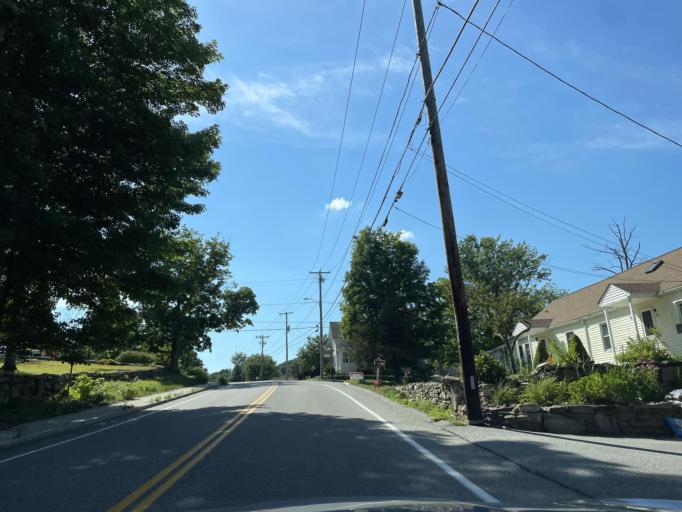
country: US
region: Massachusetts
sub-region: Worcester County
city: Northbridge
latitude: 42.1543
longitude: -71.6607
